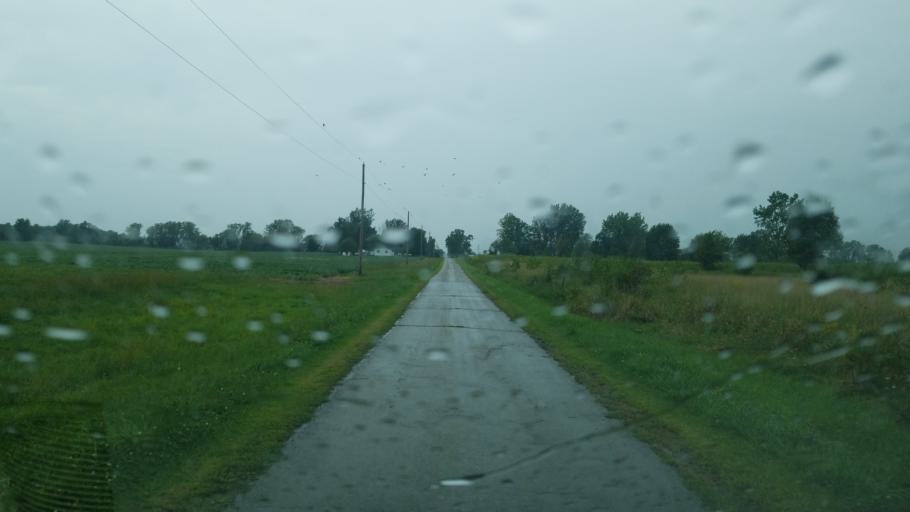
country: US
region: Ohio
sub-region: Huron County
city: Willard
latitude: 41.0101
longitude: -82.7812
